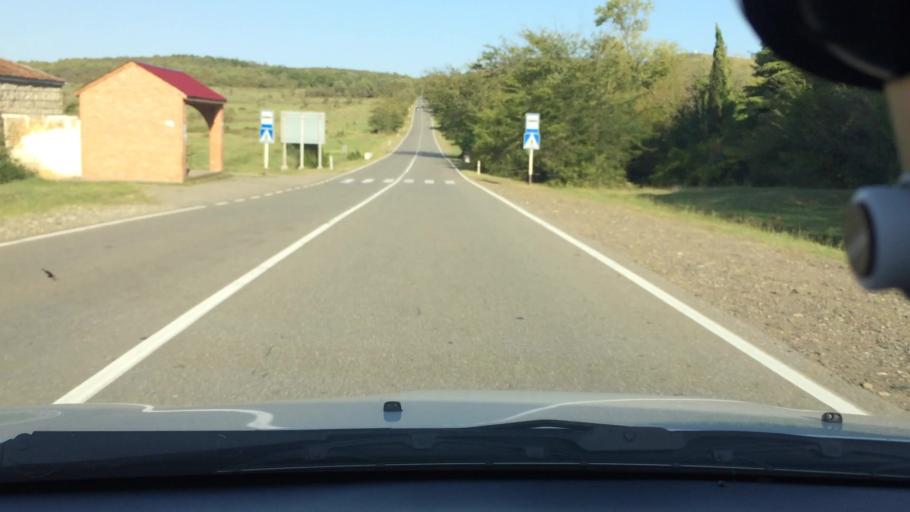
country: GE
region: Imereti
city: Kutaisi
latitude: 42.2408
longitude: 42.7649
